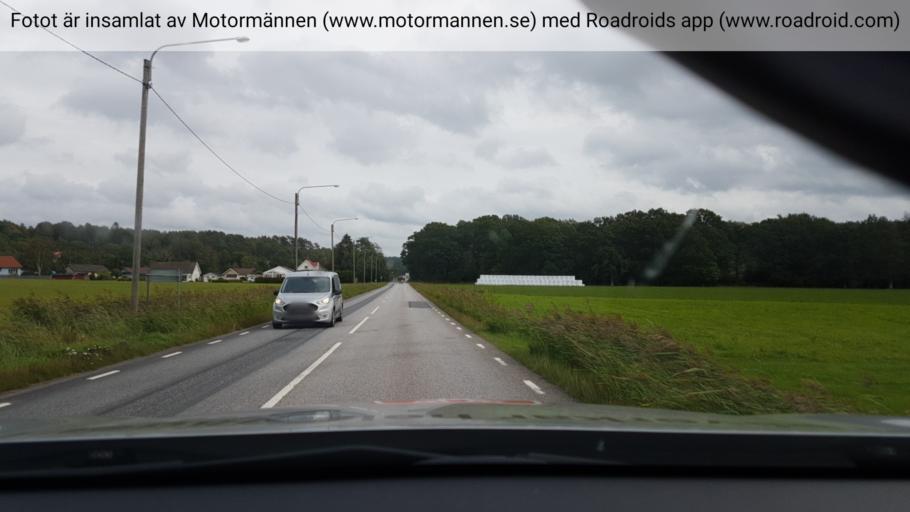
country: SE
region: Vaestra Goetaland
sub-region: Sotenas Kommun
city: Hunnebostrand
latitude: 58.5675
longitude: 11.3707
